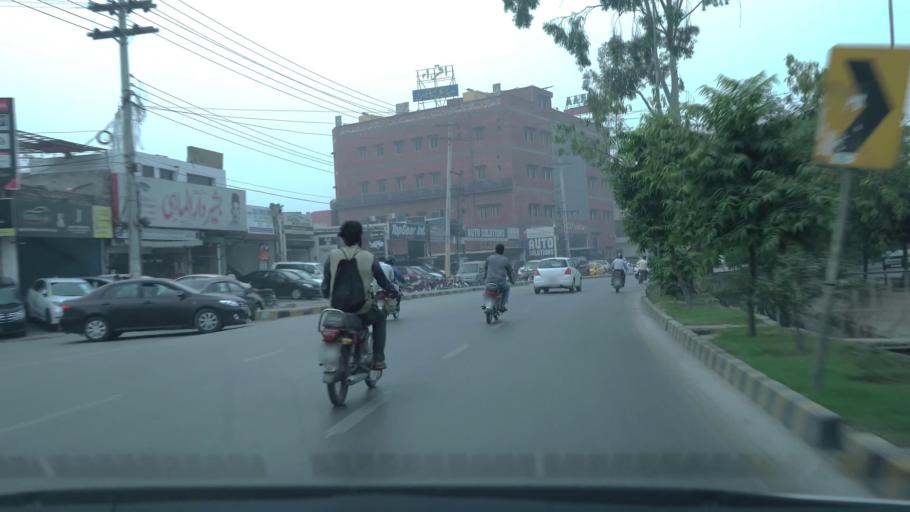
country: PK
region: Punjab
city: Lahore
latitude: 31.4711
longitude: 74.3029
